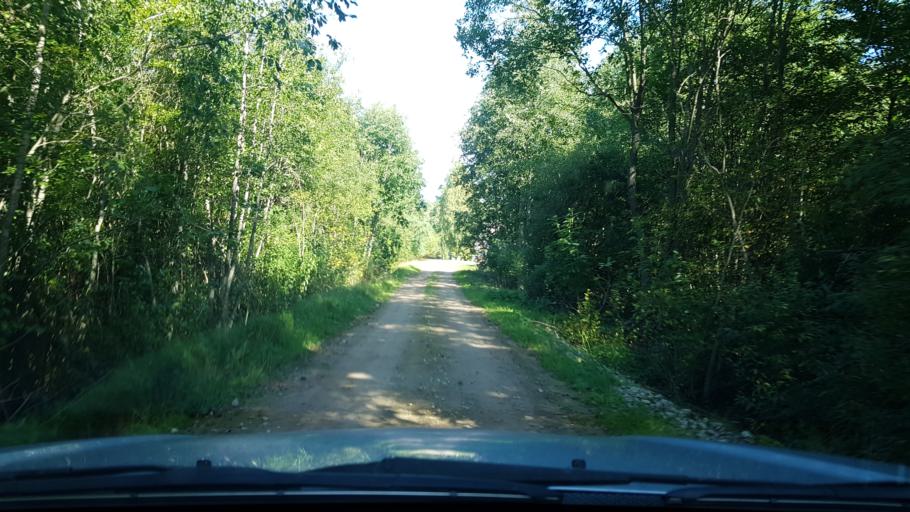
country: EE
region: Ida-Virumaa
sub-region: Sillamaee linn
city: Sillamae
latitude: 59.3448
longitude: 27.7362
